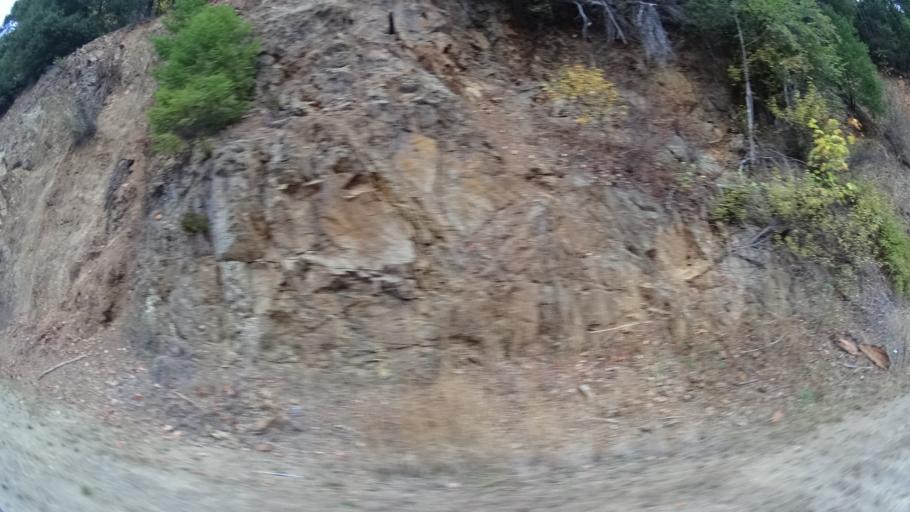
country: US
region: California
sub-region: Siskiyou County
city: Happy Camp
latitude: 41.8913
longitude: -123.4331
